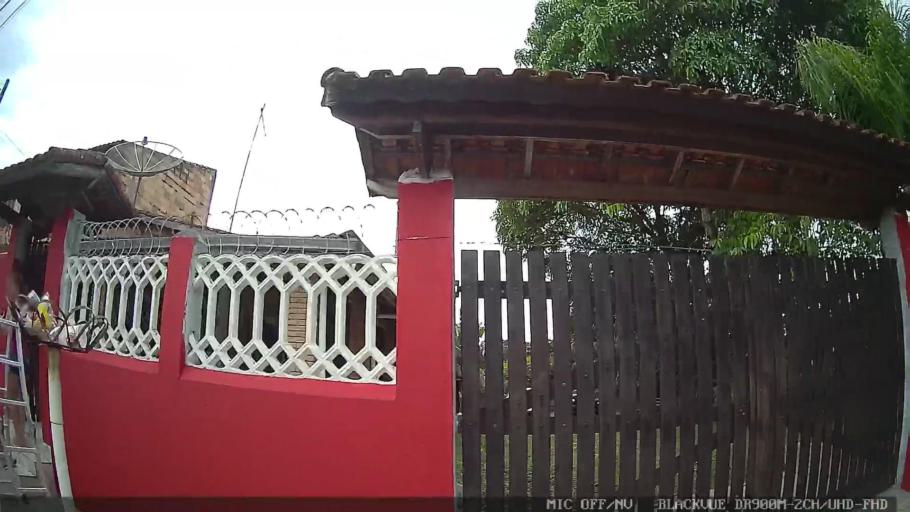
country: BR
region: Sao Paulo
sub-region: Caraguatatuba
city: Caraguatatuba
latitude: -23.6867
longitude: -45.4418
